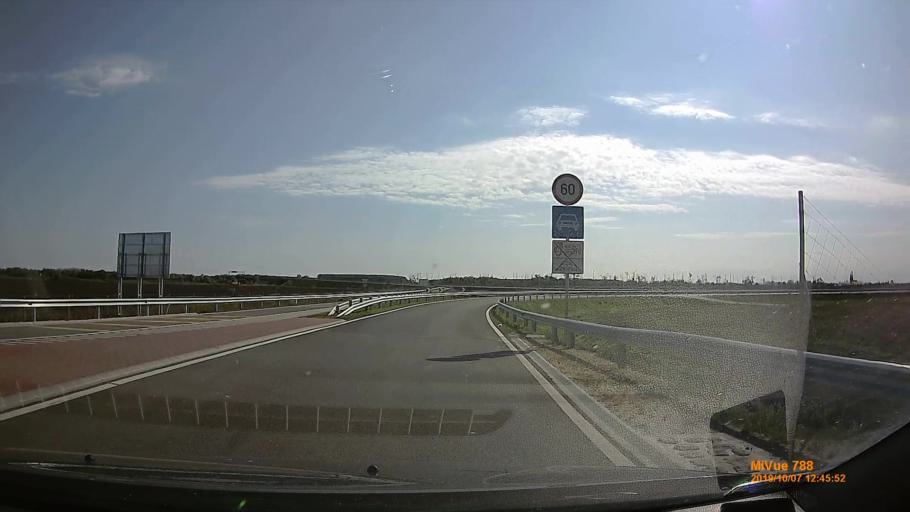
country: HU
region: Jasz-Nagykun-Szolnok
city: Kunszentmarton
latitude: 46.8730
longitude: 20.2666
